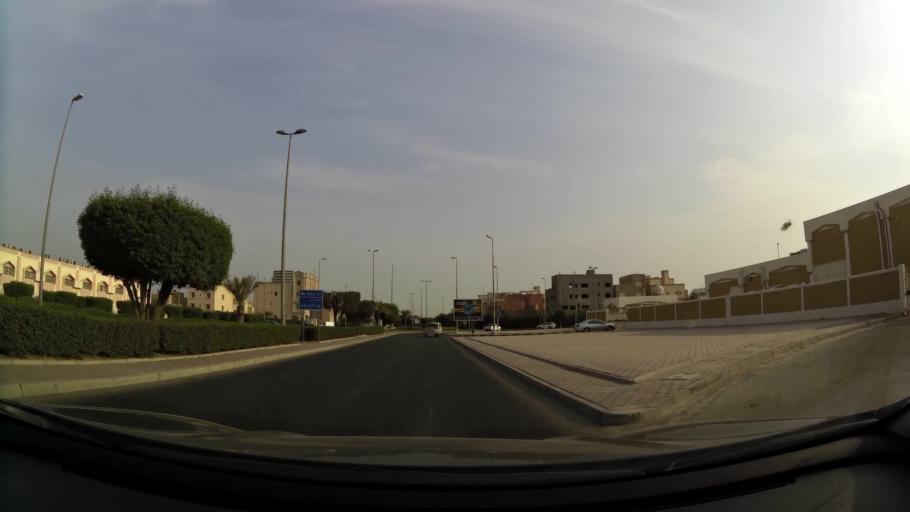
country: KW
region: Mubarak al Kabir
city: Mubarak al Kabir
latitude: 29.2131
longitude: 48.0660
